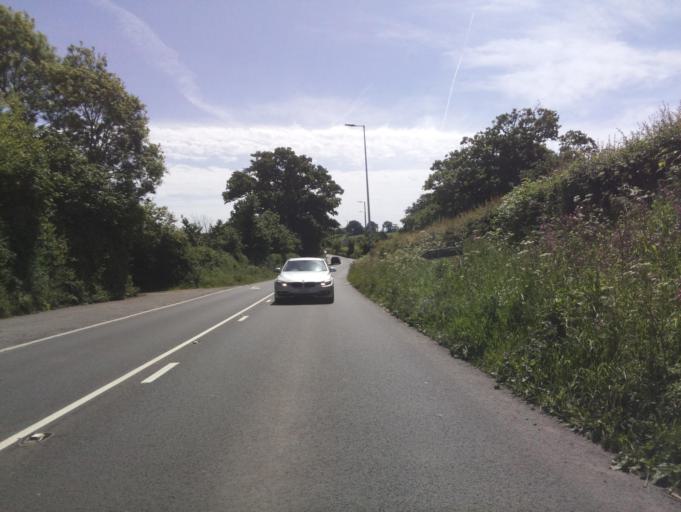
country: GB
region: England
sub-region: Devon
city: Exmouth
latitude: 50.6519
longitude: -3.4184
